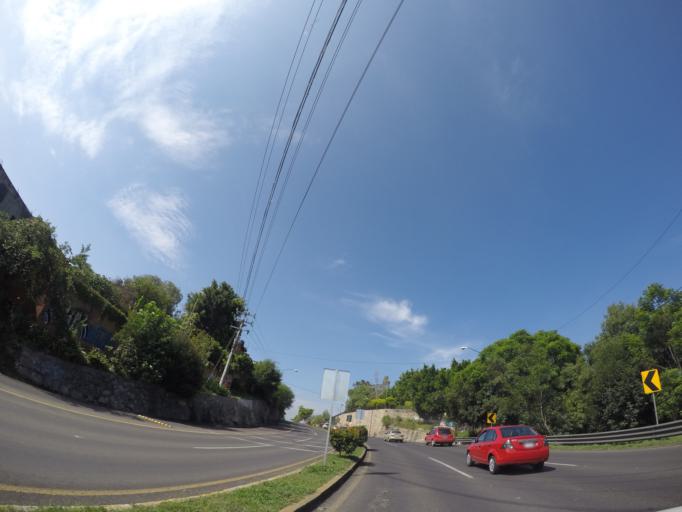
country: MX
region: Michoacan
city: Morelia
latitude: 19.6804
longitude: -101.2012
